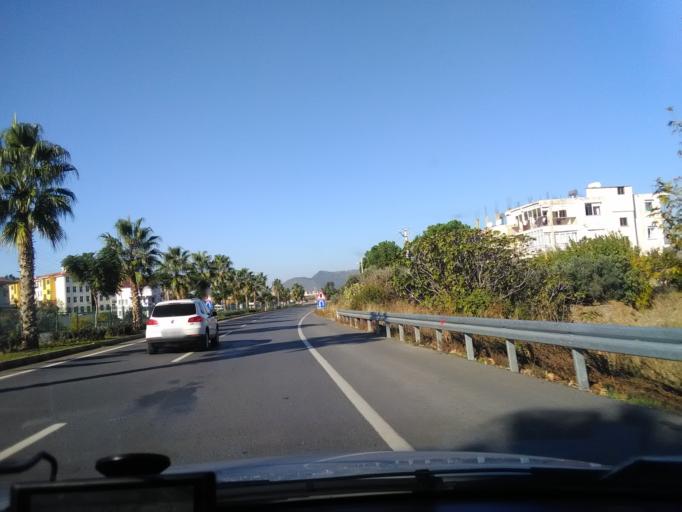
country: TR
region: Antalya
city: Gazipasa
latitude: 36.2563
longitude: 32.3290
